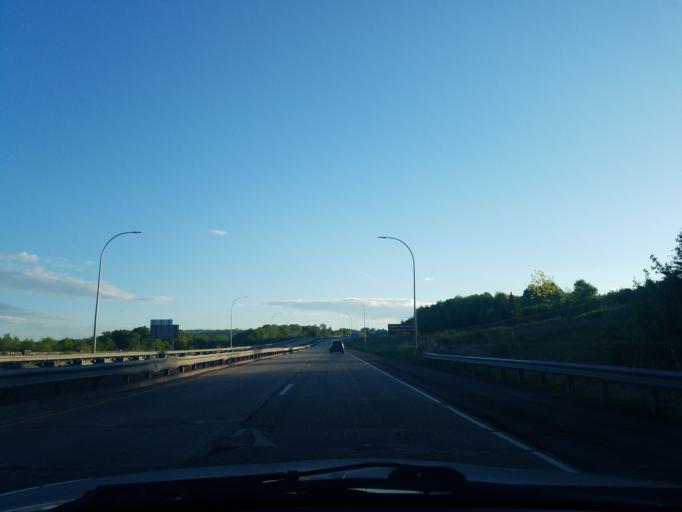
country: US
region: Minnesota
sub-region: Saint Louis County
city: Proctor
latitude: 46.7282
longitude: -92.2061
